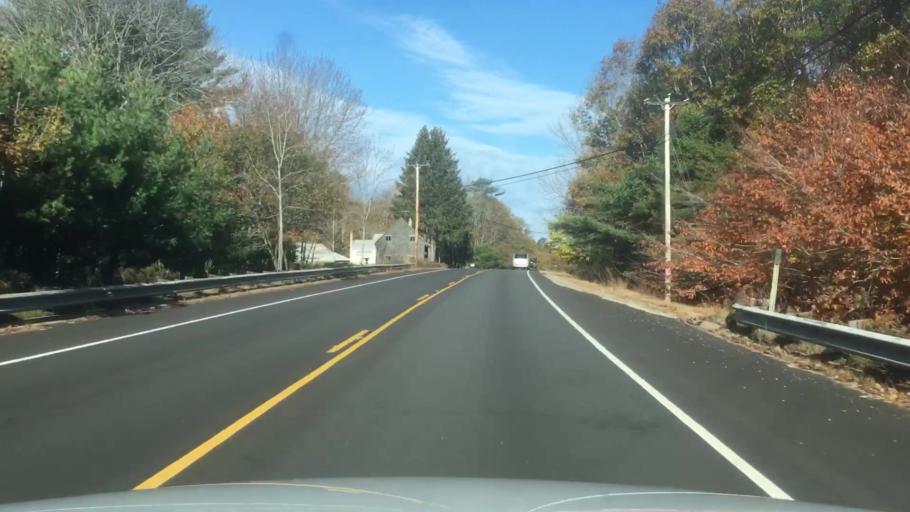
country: US
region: Maine
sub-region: Sagadahoc County
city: Woolwich
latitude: 43.8922
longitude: -69.7924
